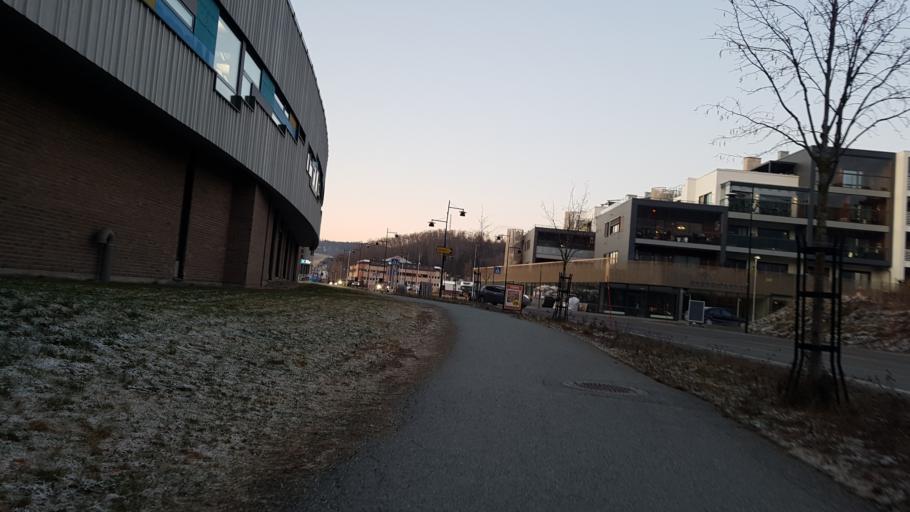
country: NO
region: Sor-Trondelag
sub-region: Melhus
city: Melhus
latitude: 63.2836
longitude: 10.2813
